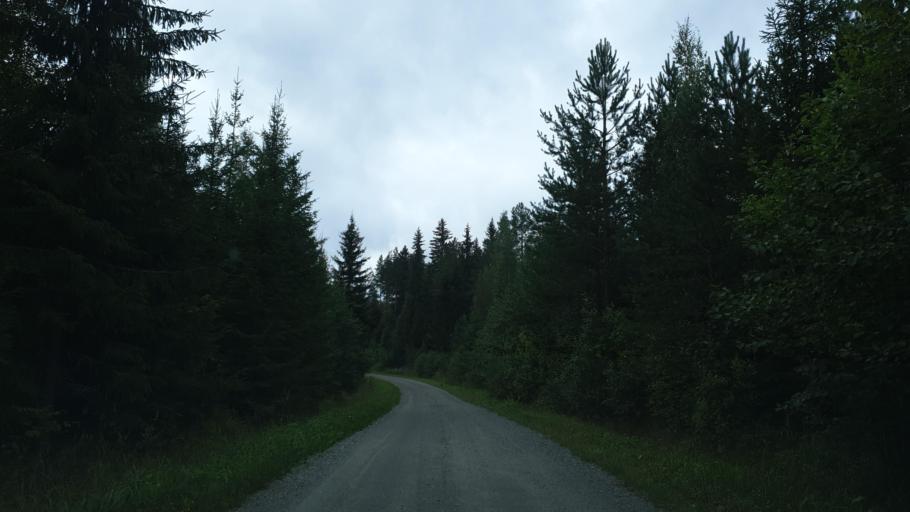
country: FI
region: Northern Savo
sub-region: Kuopio
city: Nilsiae
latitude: 63.2440
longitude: 28.2553
